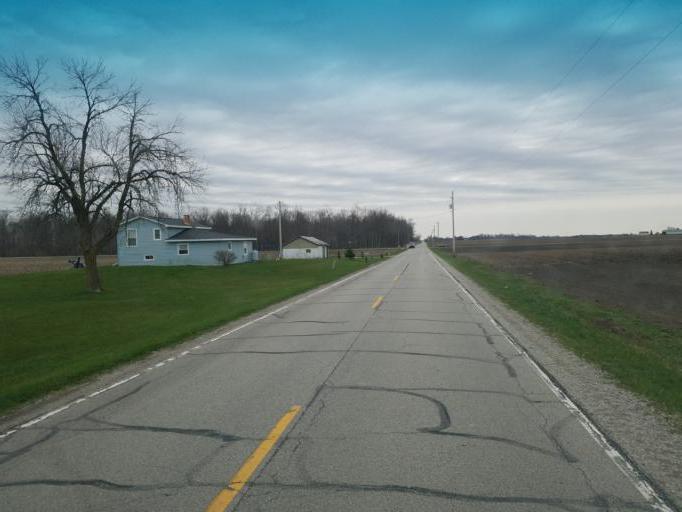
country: US
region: Ohio
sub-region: Crawford County
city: Bucyrus
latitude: 40.8583
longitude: -82.9401
